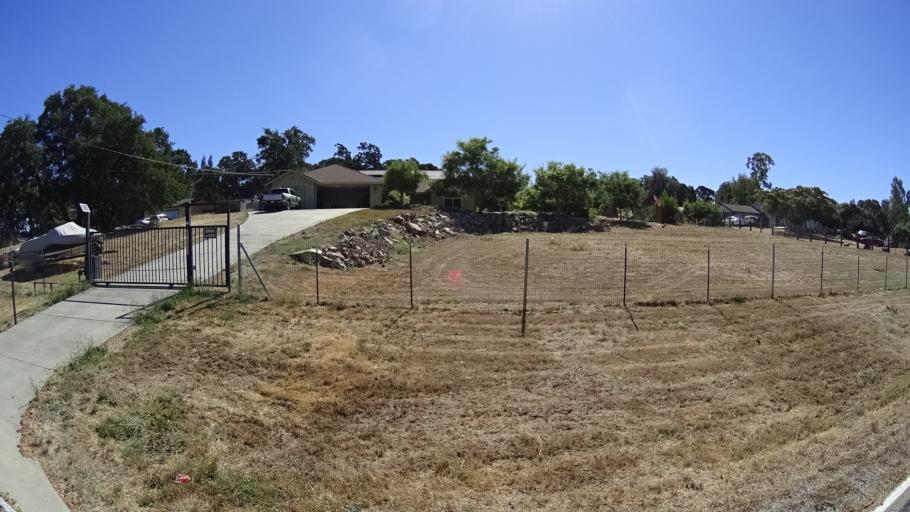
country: US
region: California
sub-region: Calaveras County
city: Rancho Calaveras
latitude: 38.1074
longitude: -120.8740
